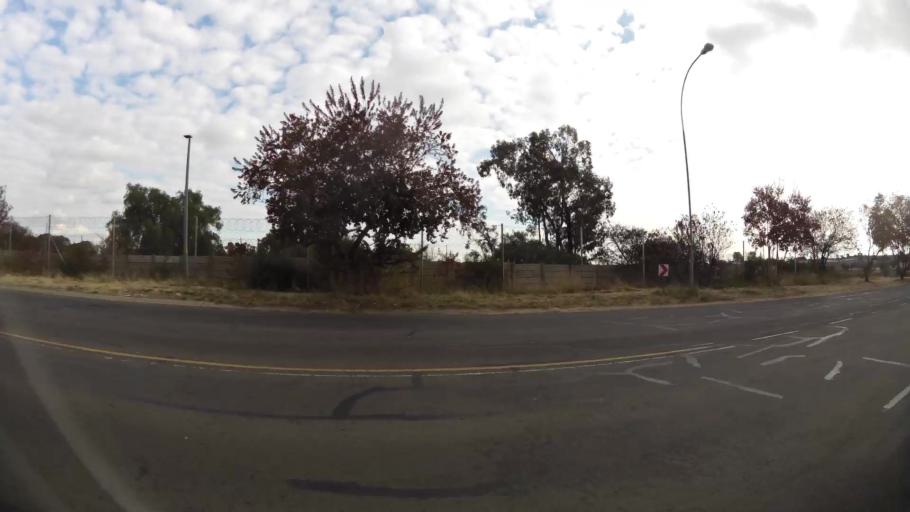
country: ZA
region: Orange Free State
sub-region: Mangaung Metropolitan Municipality
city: Bloemfontein
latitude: -29.0786
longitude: 26.1948
